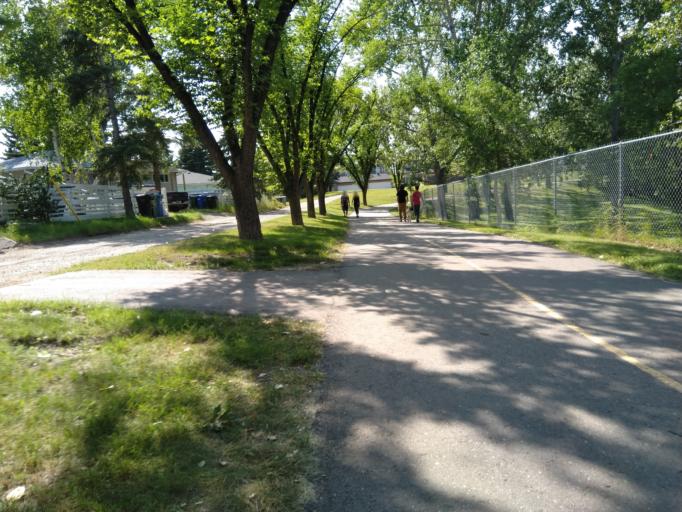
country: CA
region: Alberta
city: Calgary
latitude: 51.0771
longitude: -114.1027
